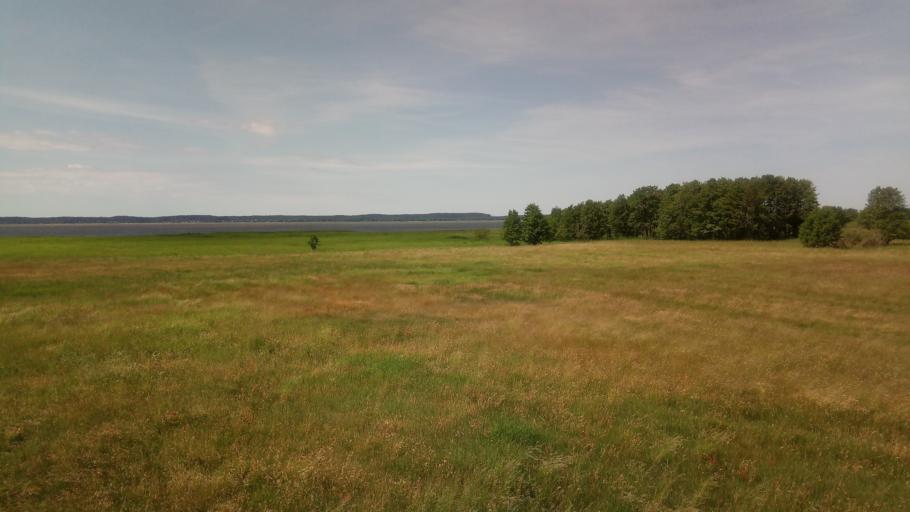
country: LT
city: Priekule
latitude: 55.5454
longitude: 21.2110
